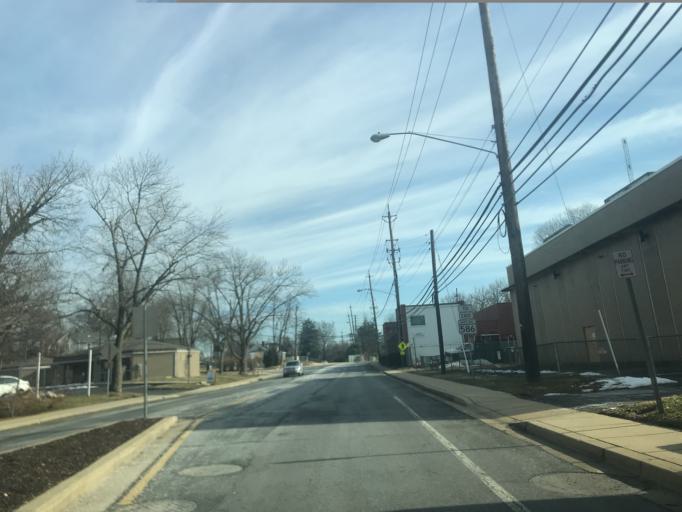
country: US
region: Maryland
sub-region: Montgomery County
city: Rockville
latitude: 39.0827
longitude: -77.1434
